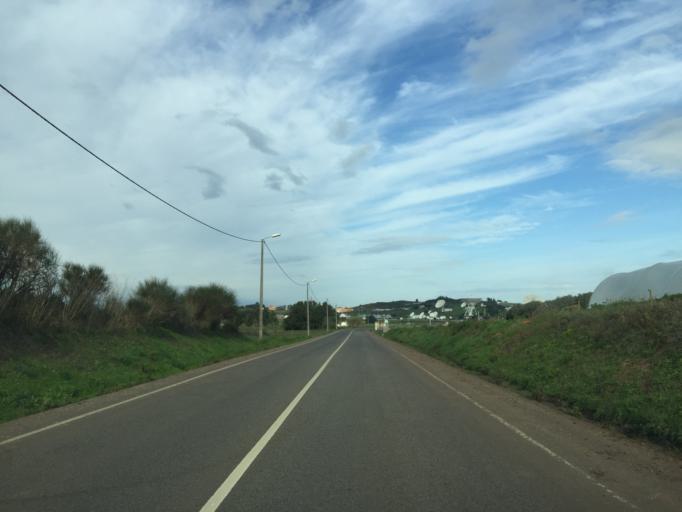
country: PT
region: Lisbon
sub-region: Sintra
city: Almargem
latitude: 38.8600
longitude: -9.2781
